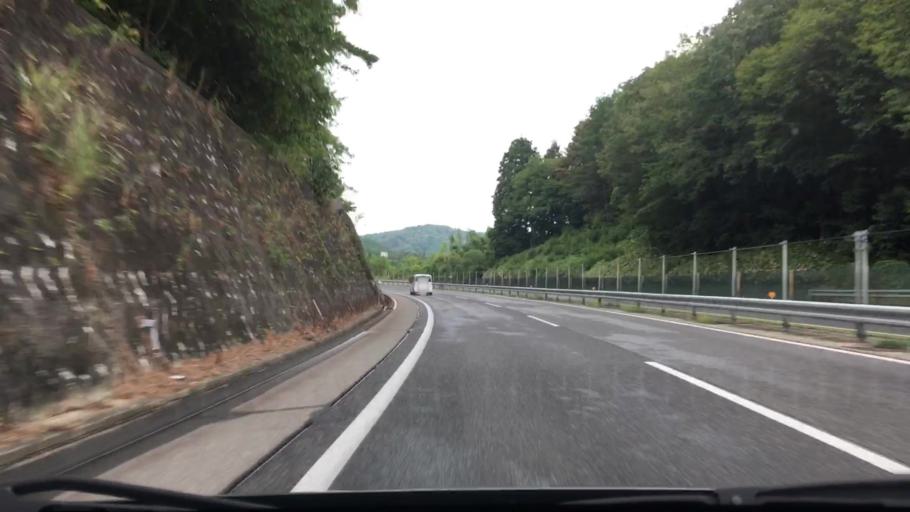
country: JP
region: Hiroshima
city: Miyoshi
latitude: 34.7186
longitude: 132.6447
